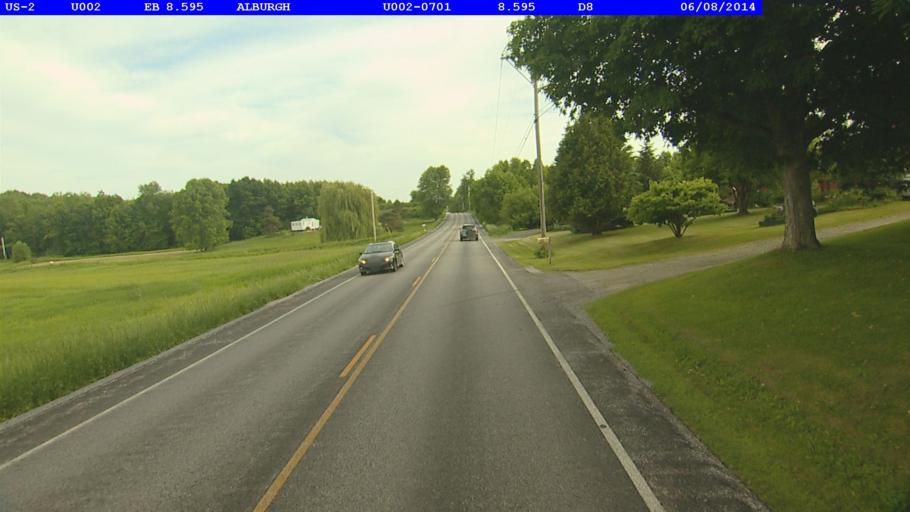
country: US
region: Vermont
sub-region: Grand Isle County
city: North Hero
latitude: 44.9268
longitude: -73.2744
